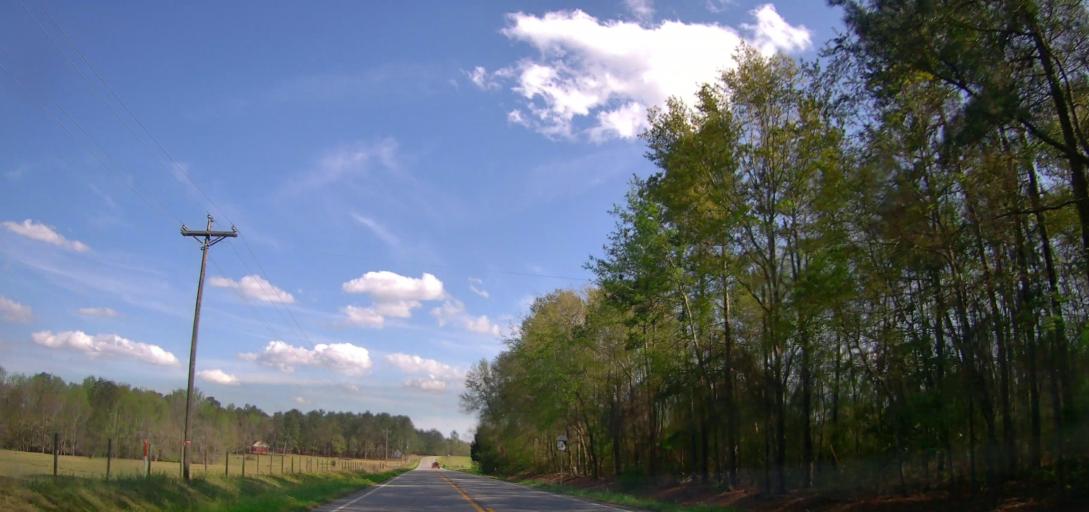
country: US
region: Georgia
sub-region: Baldwin County
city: Hardwick
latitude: 33.0590
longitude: -83.1287
